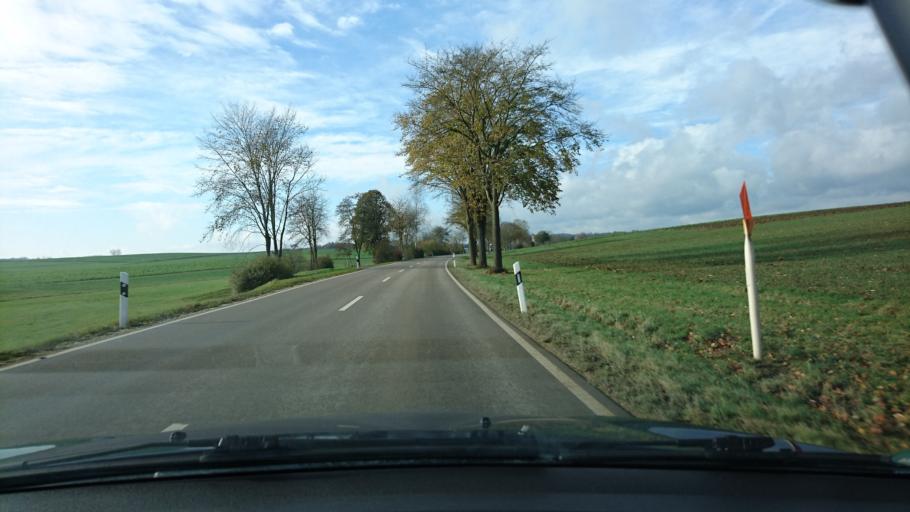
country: DE
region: Bavaria
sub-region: Swabia
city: Amerdingen
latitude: 48.7257
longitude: 10.5041
